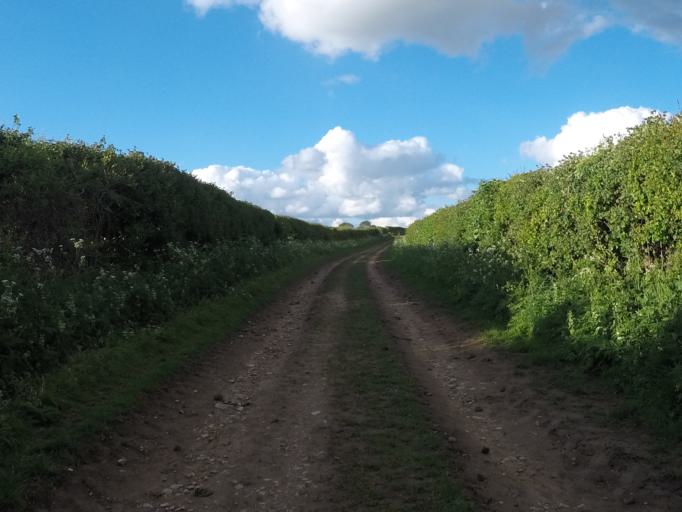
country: GB
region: England
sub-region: Oxfordshire
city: Charlbury
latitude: 51.8549
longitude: -1.4611
